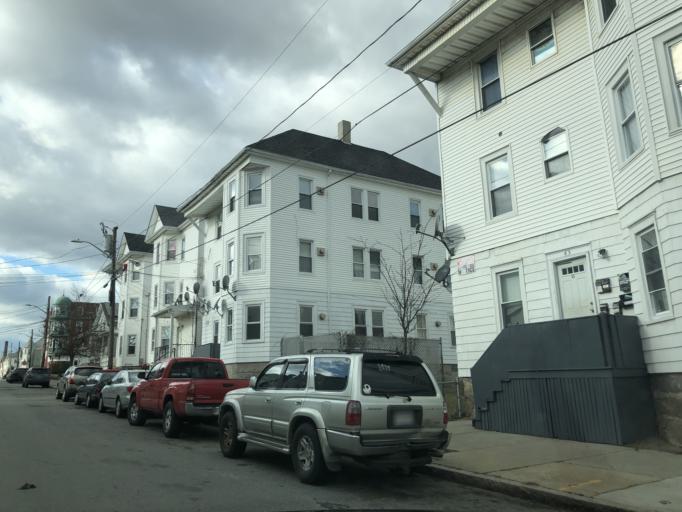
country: US
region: Massachusetts
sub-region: Bristol County
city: New Bedford
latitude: 41.6593
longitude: -70.9261
